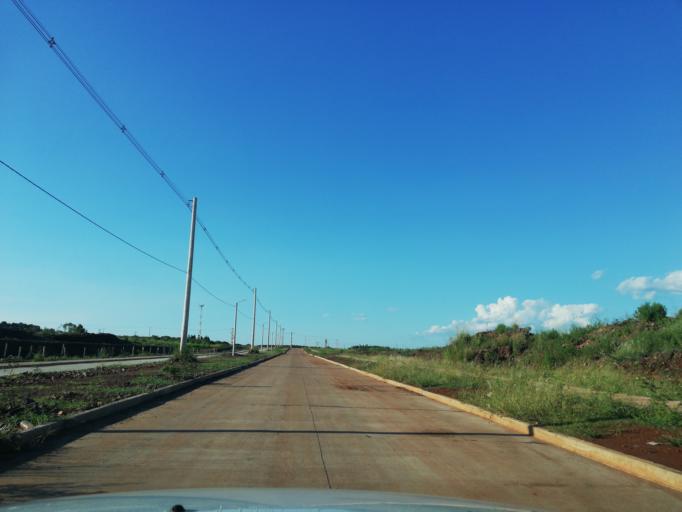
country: AR
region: Misiones
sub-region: Departamento de Capital
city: Posadas
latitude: -27.3963
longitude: -55.9902
